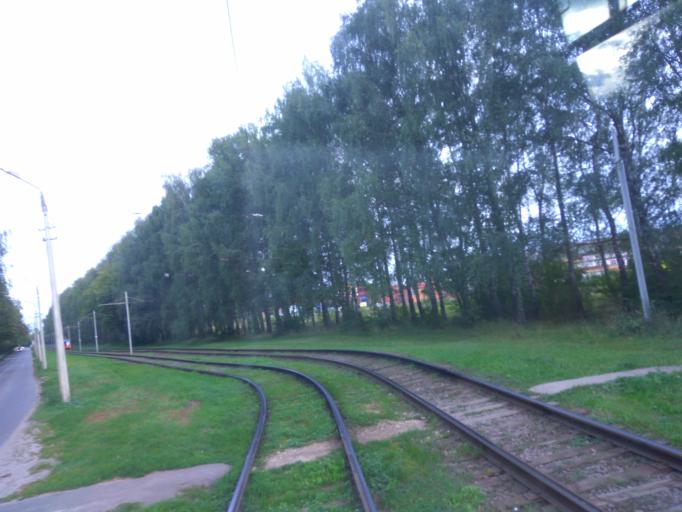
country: RU
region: Moskovskaya
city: Kolomna
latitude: 55.0737
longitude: 38.7870
